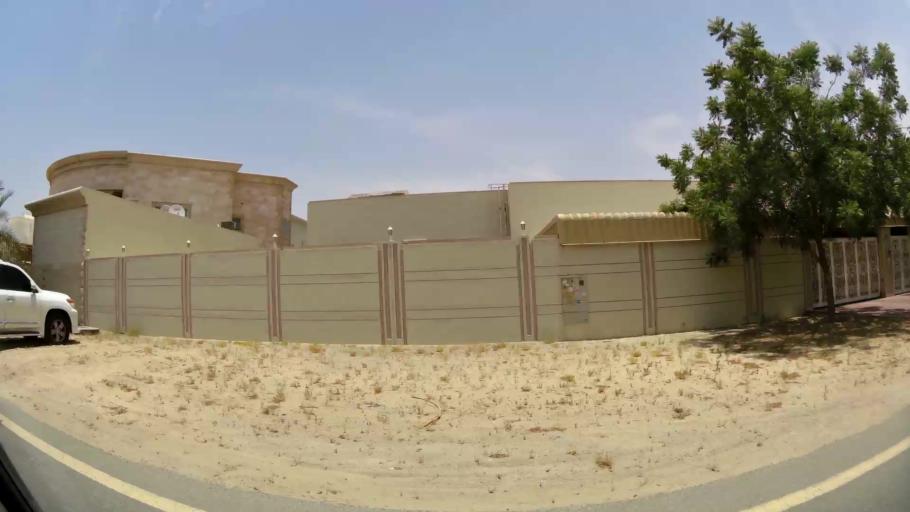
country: AE
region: Ash Shariqah
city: Sharjah
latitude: 25.2350
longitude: 55.4563
